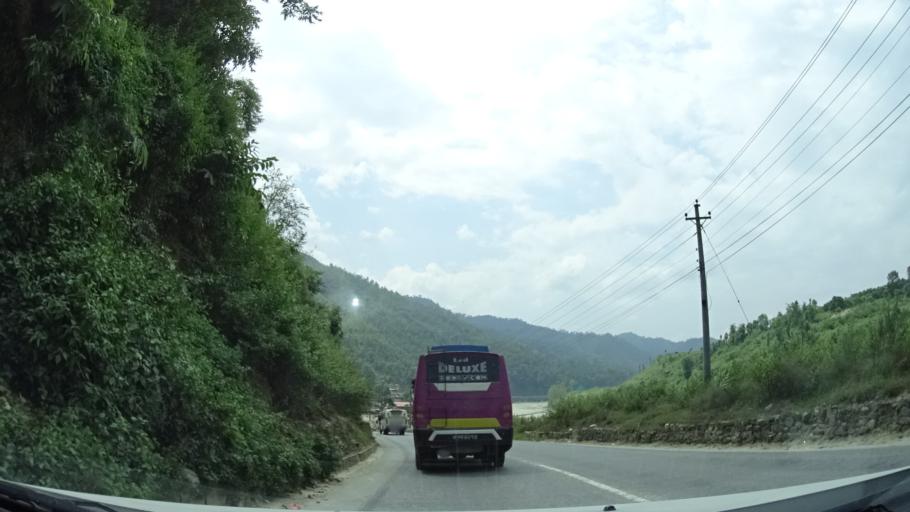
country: NP
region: Central Region
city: Kirtipur
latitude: 27.8006
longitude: 84.9310
